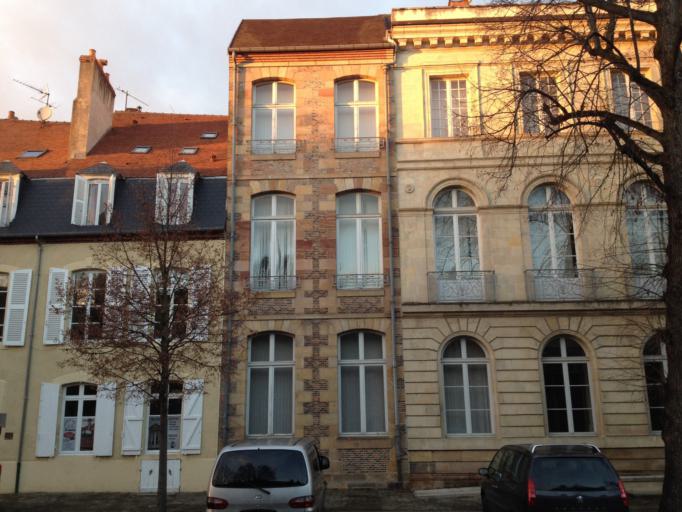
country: FR
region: Auvergne
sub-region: Departement de l'Allier
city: Moulins
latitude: 46.5679
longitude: 3.3317
